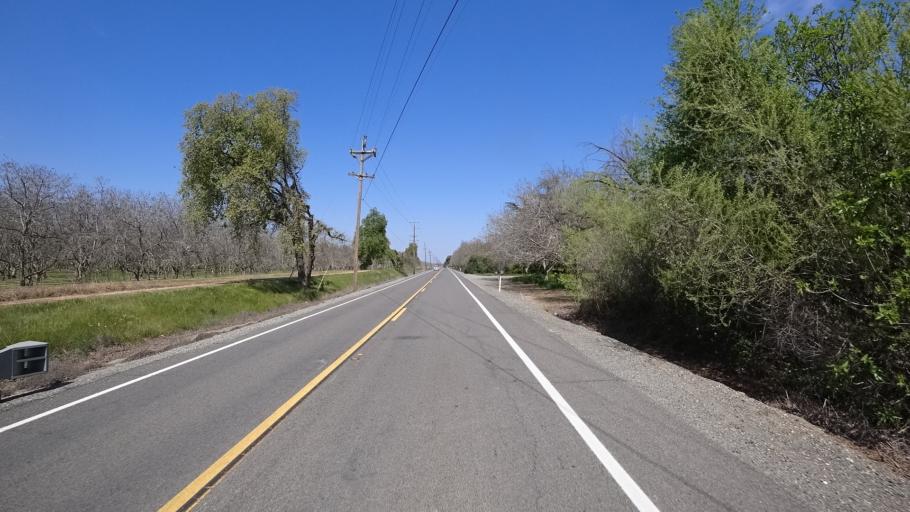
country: US
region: California
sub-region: Glenn County
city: Willows
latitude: 39.4769
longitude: -122.0187
